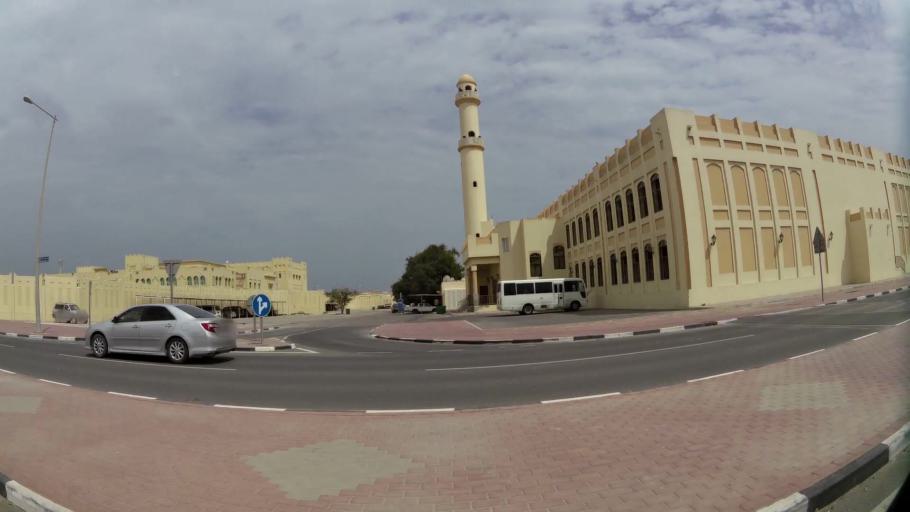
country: QA
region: Baladiyat ar Rayyan
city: Ar Rayyan
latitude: 25.3261
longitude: 51.4722
